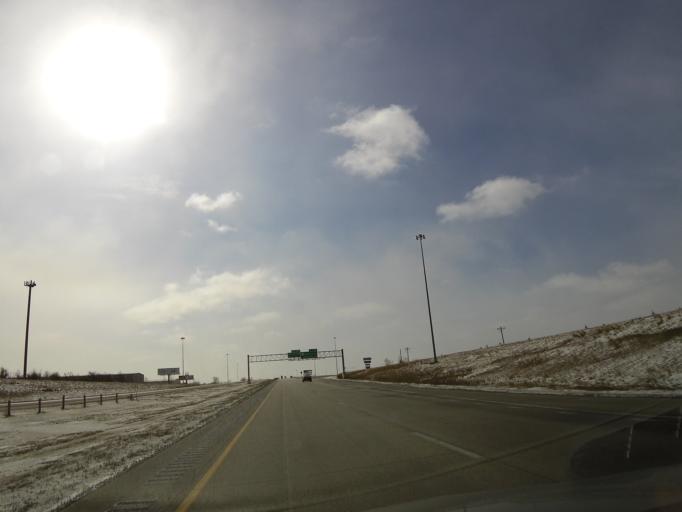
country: US
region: North Dakota
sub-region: Grand Forks County
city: Grand Forks
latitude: 47.9397
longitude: -97.0937
